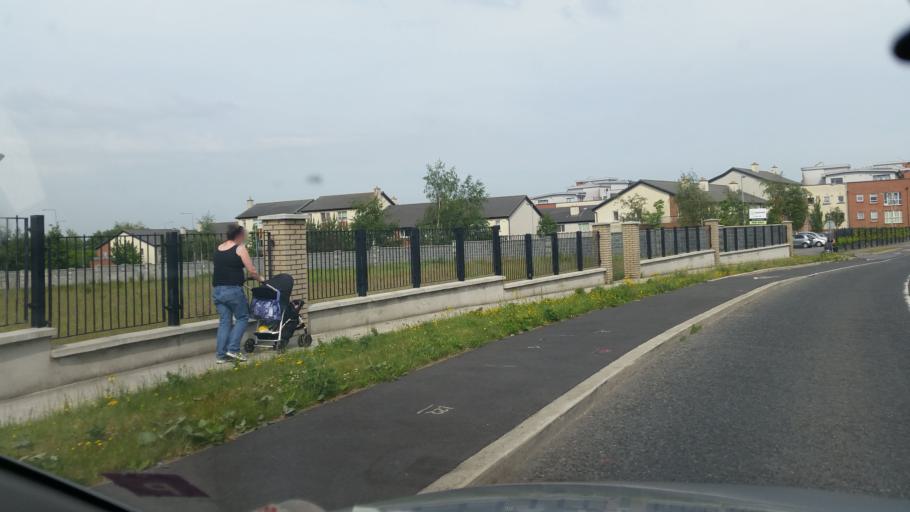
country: IE
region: Leinster
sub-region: Dublin City
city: Finglas
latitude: 53.4067
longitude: -6.2909
